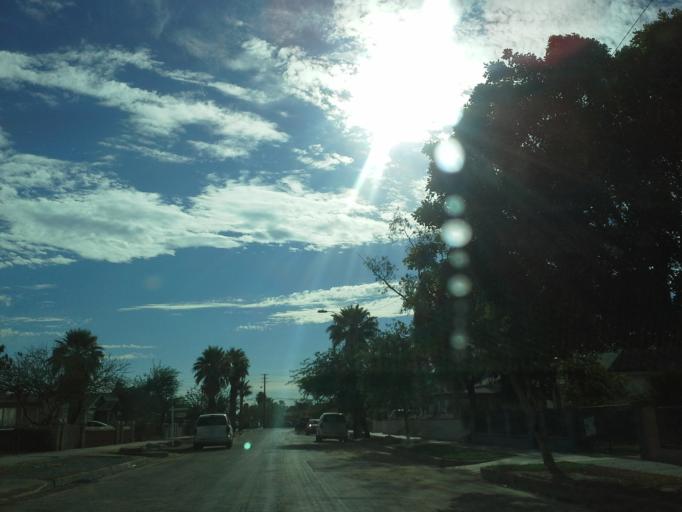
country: US
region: Arizona
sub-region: Maricopa County
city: Phoenix
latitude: 33.4542
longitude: -112.0897
